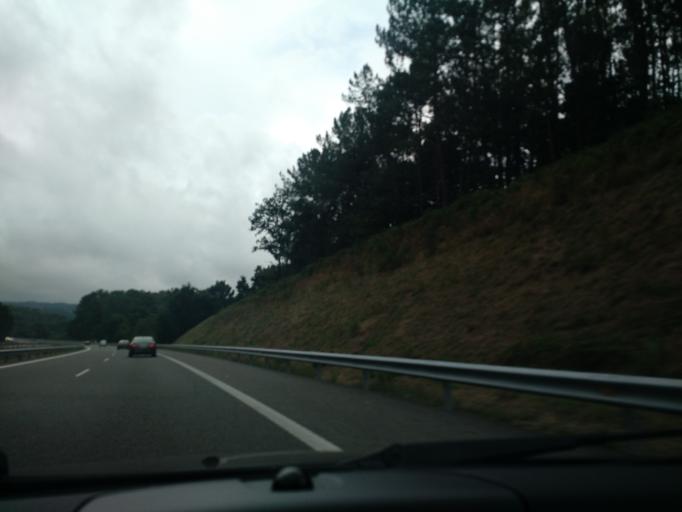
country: ES
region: Galicia
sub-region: Provincia da Coruna
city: Abegondo
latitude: 43.2295
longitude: -8.2691
